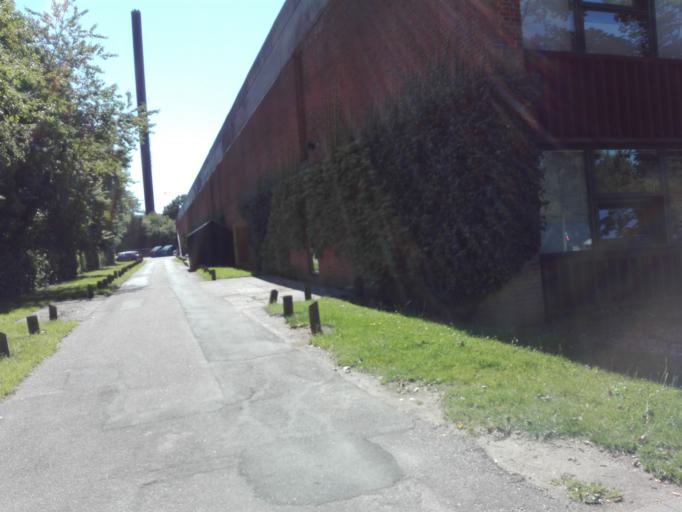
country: DK
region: Central Jutland
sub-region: Arhus Kommune
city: Tranbjerg
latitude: 56.1082
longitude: 10.1430
